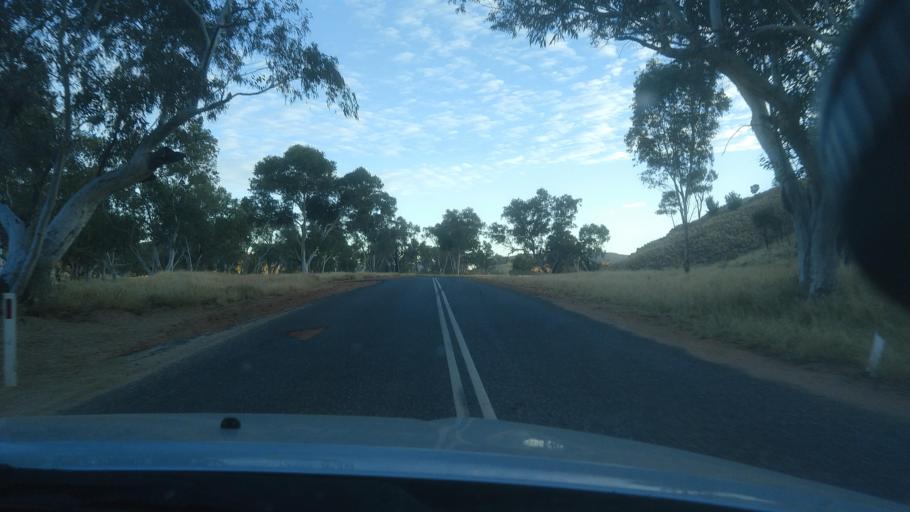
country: AU
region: Northern Territory
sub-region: Alice Springs
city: Alice Springs
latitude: -23.7394
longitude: 133.7422
